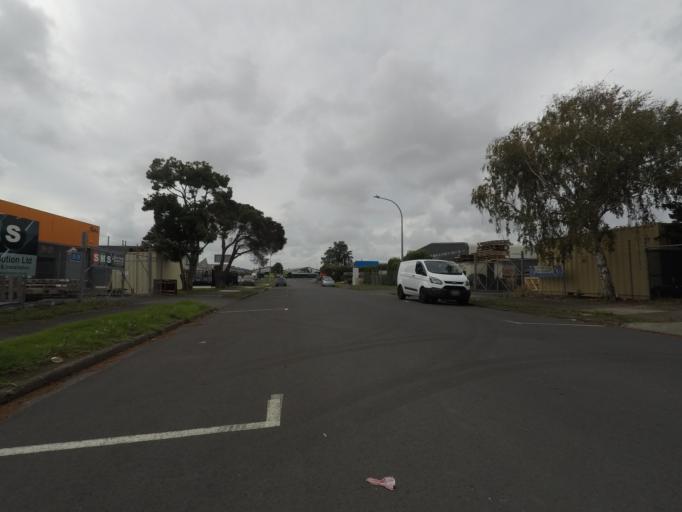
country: NZ
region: Auckland
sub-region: Auckland
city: Rosebank
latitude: -36.8831
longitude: 174.6770
